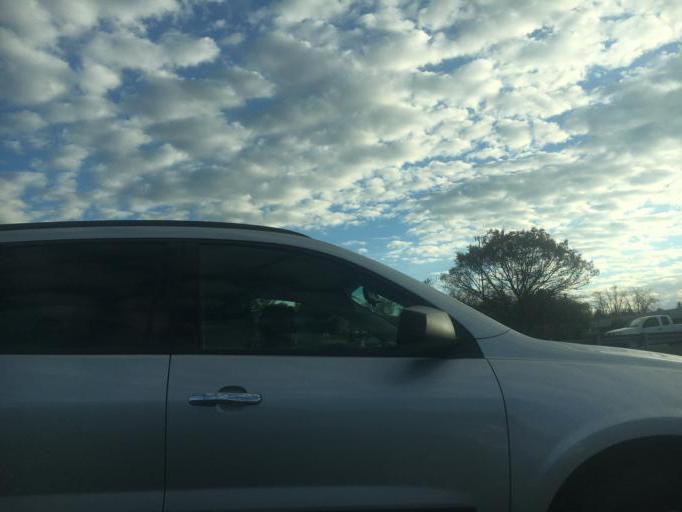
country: US
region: Virginia
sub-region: Washington County
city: Abingdon
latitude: 36.6999
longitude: -81.9767
